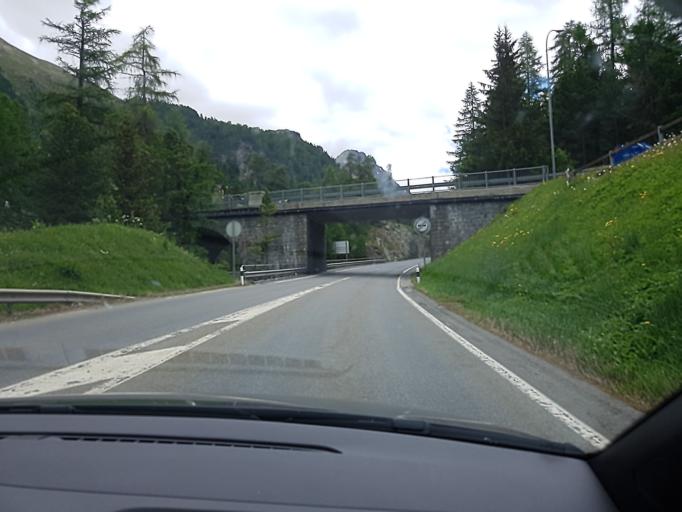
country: CH
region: Grisons
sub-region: Maloja District
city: Pontresina
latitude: 46.4907
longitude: 9.9013
